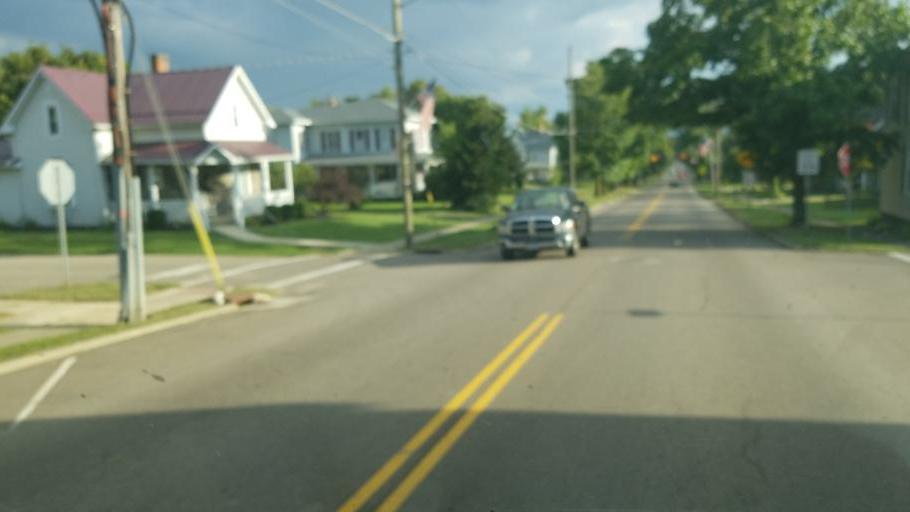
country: US
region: Ohio
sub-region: Knox County
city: Danville
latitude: 40.4504
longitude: -82.2603
